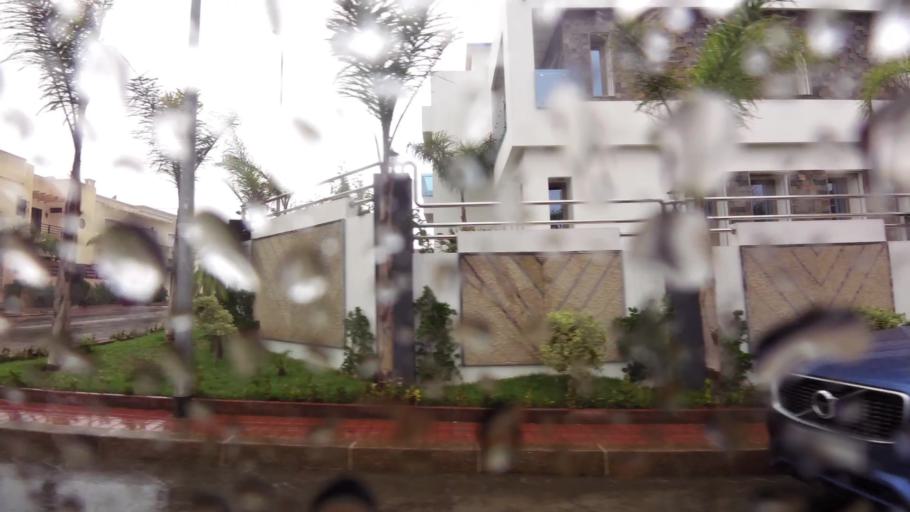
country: MA
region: Grand Casablanca
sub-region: Casablanca
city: Casablanca
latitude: 33.5431
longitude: -7.6684
